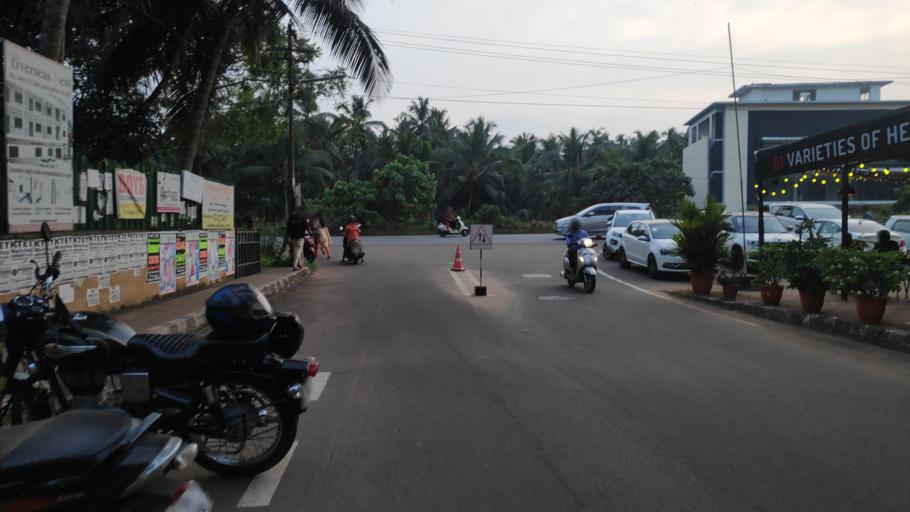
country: IN
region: Kerala
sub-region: Kozhikode
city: Kozhikode
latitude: 11.2534
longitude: 75.8273
